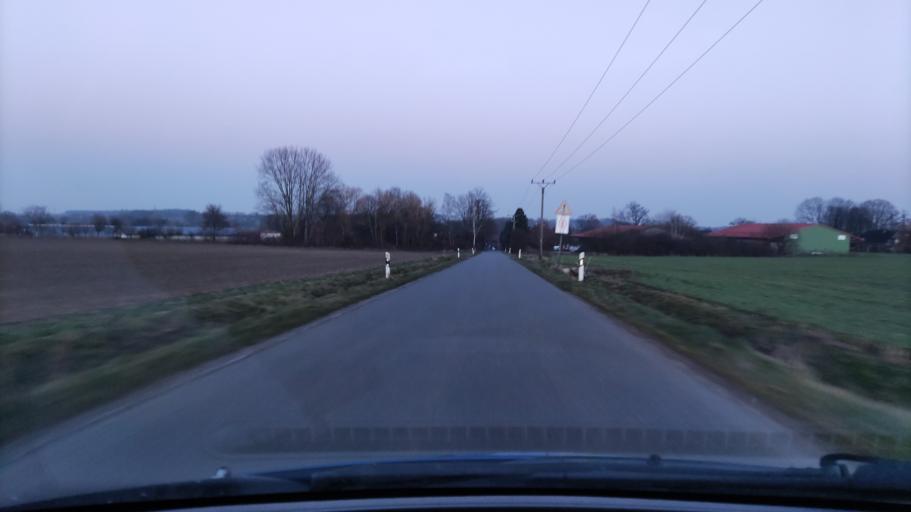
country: DE
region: Lower Saxony
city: Barum
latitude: 53.0524
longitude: 10.5070
